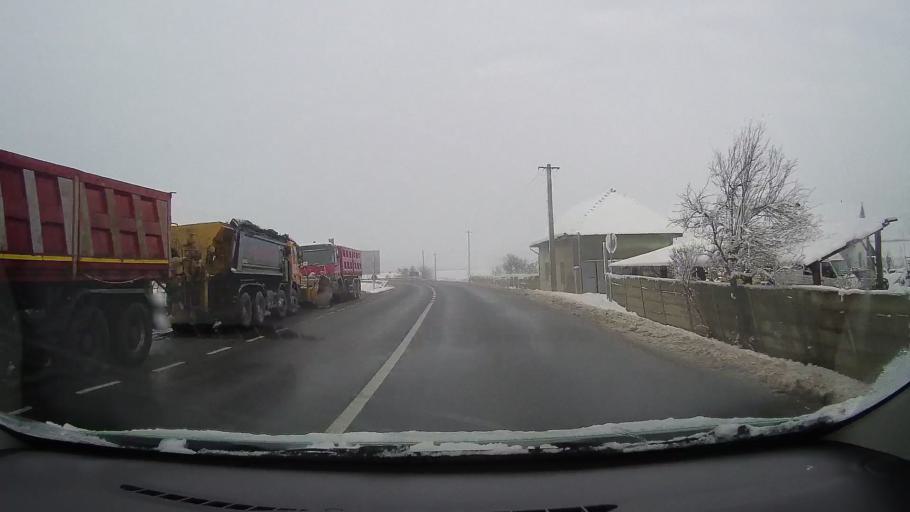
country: RO
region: Alba
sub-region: Municipiul Sebes
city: Lancram
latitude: 45.9818
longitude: 23.5178
